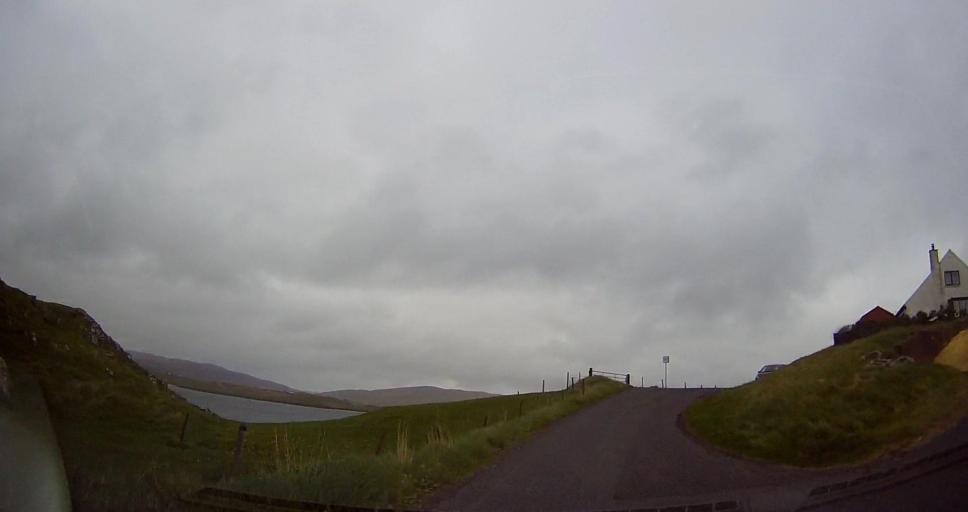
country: GB
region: Scotland
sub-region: Shetland Islands
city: Lerwick
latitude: 60.3753
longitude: -1.3837
